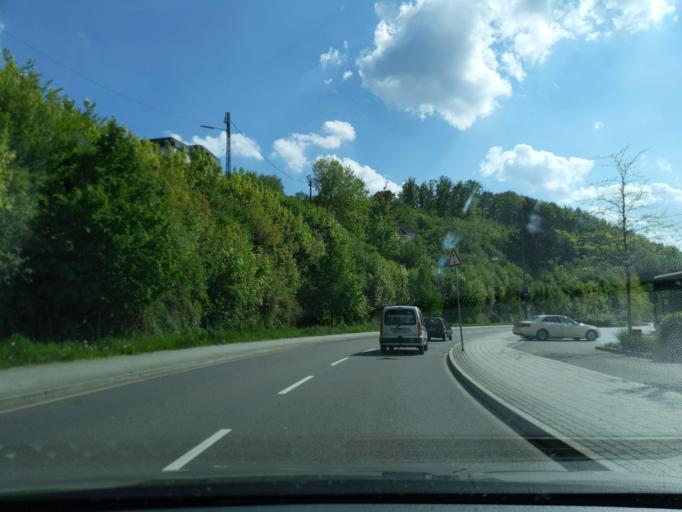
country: DE
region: North Rhine-Westphalia
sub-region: Regierungsbezirk Koln
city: Gummersbach
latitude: 51.0235
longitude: 7.5672
